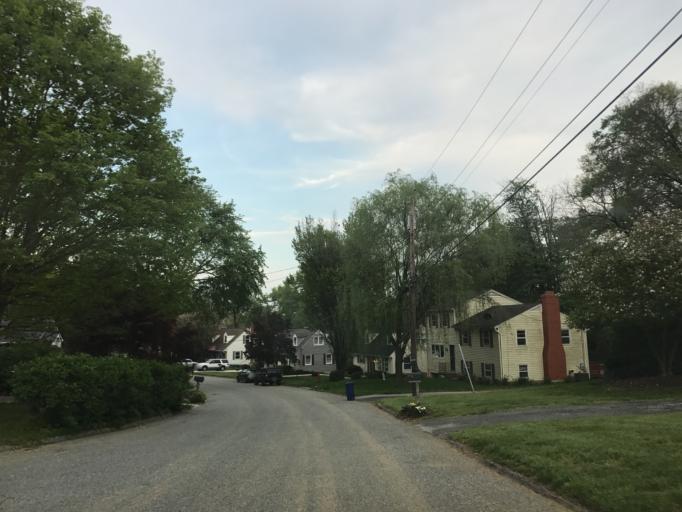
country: US
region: Maryland
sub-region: Baltimore County
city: Cockeysville
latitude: 39.4772
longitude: -76.6318
